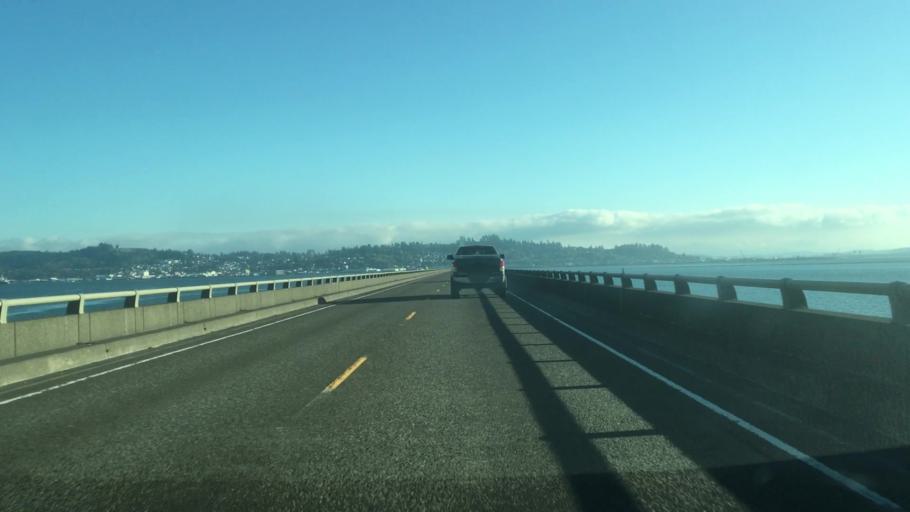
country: US
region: Oregon
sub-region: Clatsop County
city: Astoria
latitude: 46.2197
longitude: -123.8646
